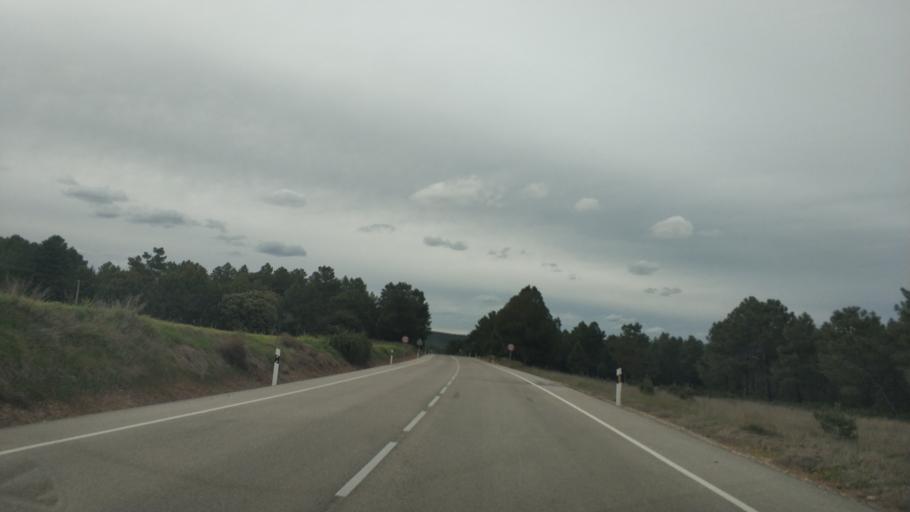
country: ES
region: Castille and Leon
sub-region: Provincia de Soria
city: Valdenebro
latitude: 41.5497
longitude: -2.9615
